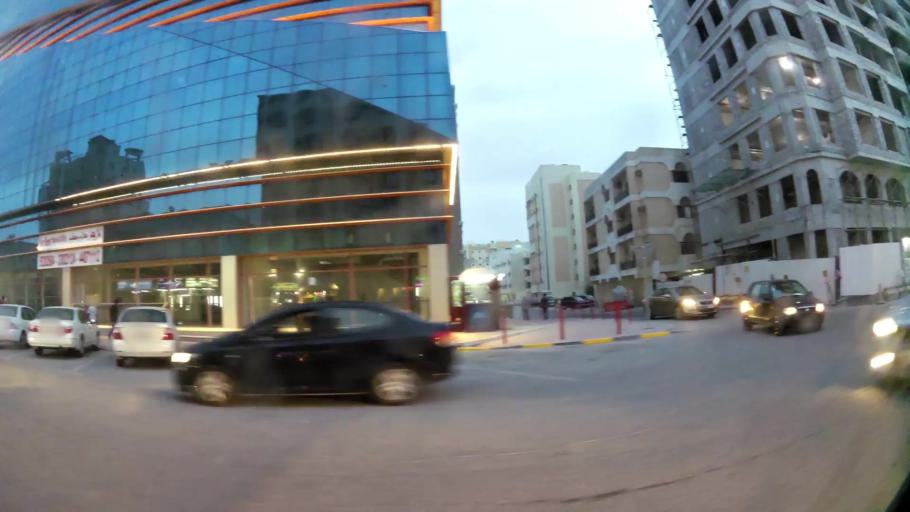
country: QA
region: Baladiyat ad Dawhah
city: Doha
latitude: 25.2723
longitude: 51.5258
